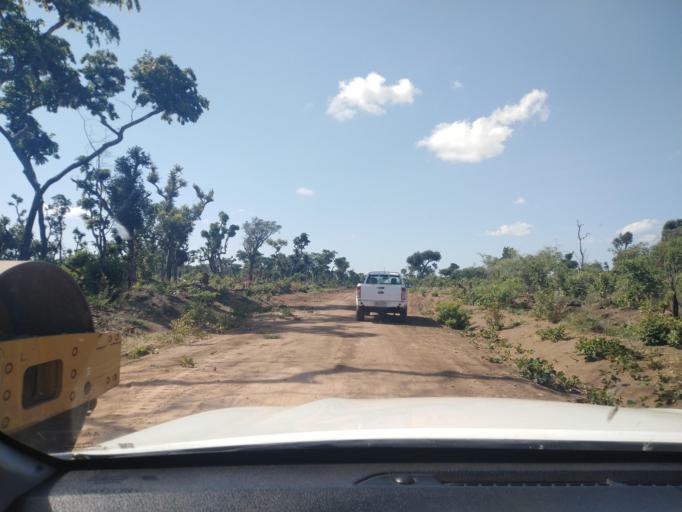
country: ZM
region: Northern
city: Chinsali
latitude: -11.0096
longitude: 31.7741
